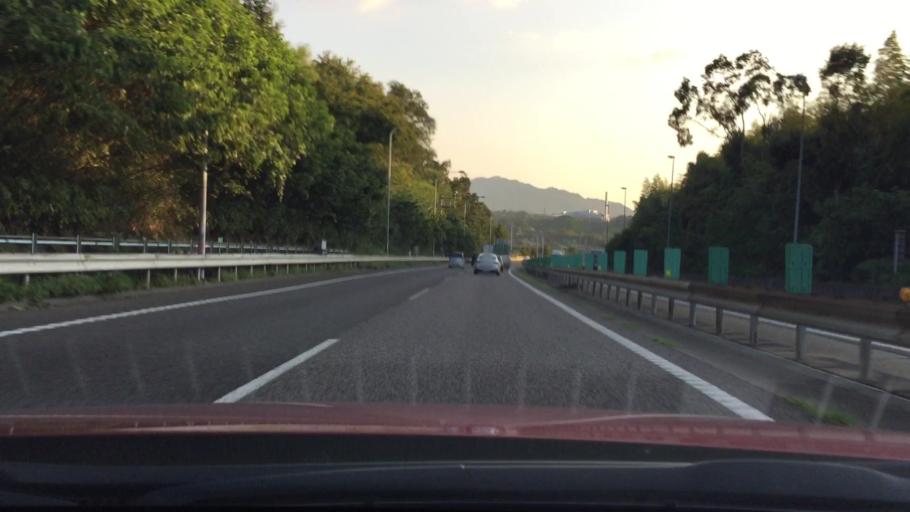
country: JP
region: Shiga Prefecture
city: Moriyama
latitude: 35.0316
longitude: 136.0438
